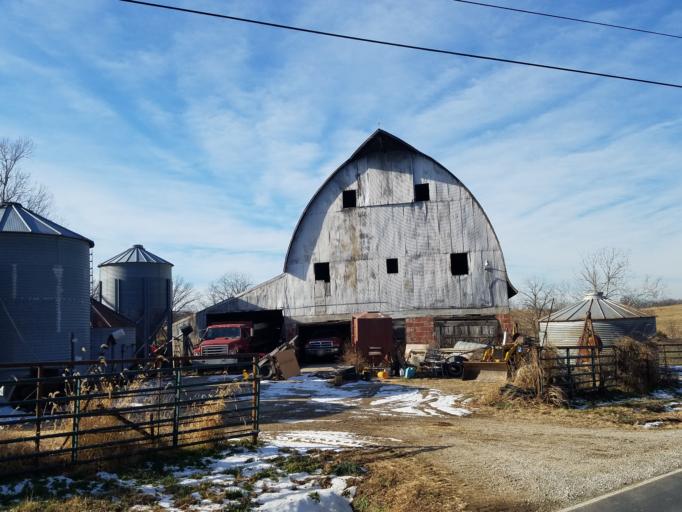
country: US
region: Missouri
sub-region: Cole County
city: Saint Martins
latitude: 38.6913
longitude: -92.3658
